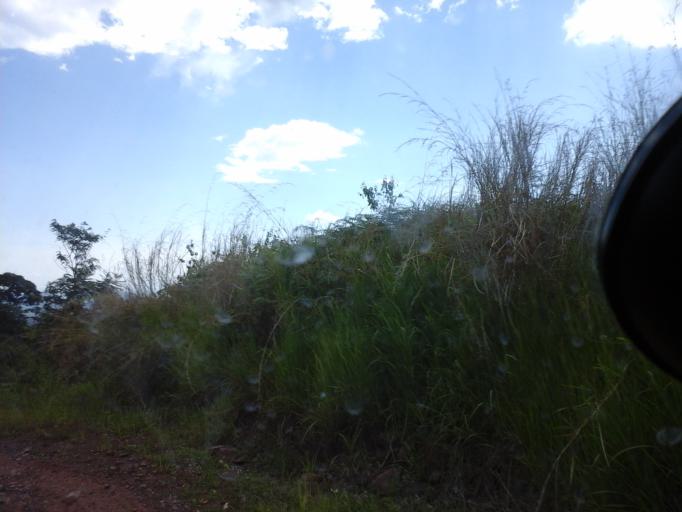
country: CO
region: Cesar
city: San Diego
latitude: 10.2709
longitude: -73.0814
